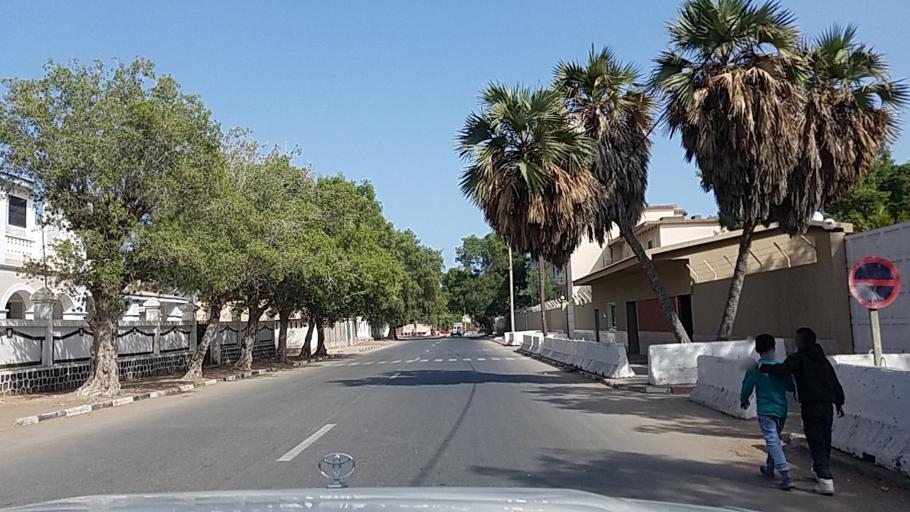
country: DJ
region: Djibouti
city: Djibouti
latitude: 11.6029
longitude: 43.1546
